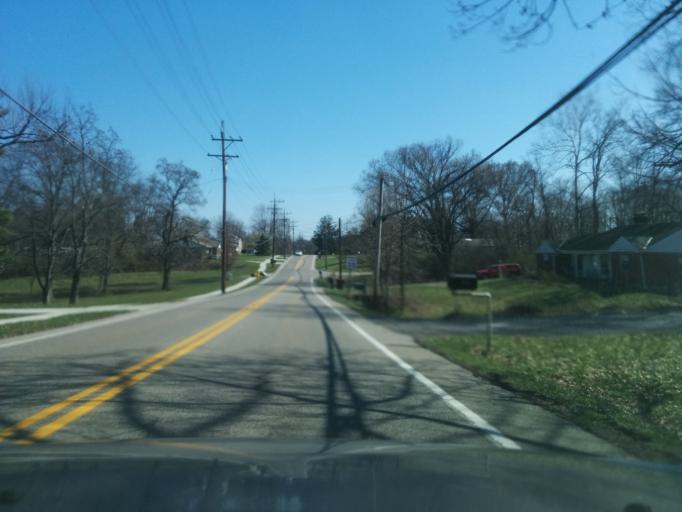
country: US
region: Ohio
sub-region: Hamilton County
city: Northgate
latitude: 39.2360
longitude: -84.6091
